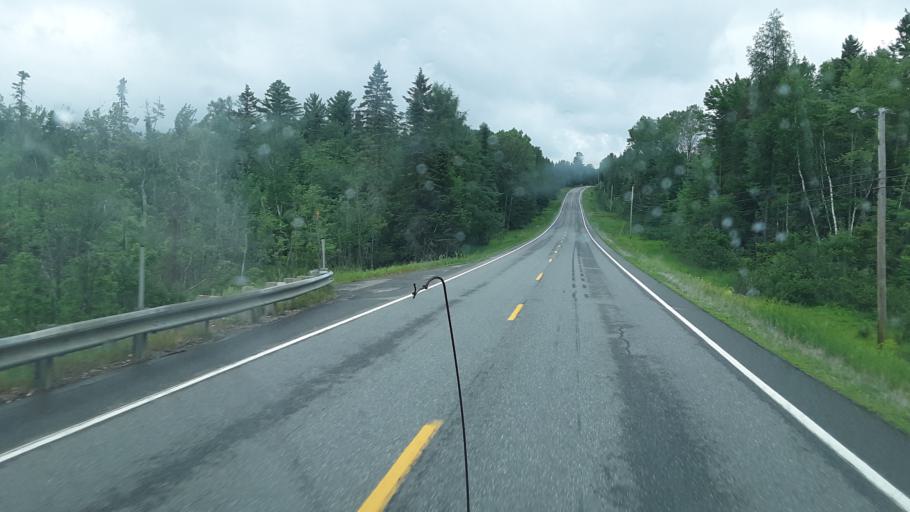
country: US
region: Maine
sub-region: Aroostook County
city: Presque Isle
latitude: 46.4712
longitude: -68.3887
